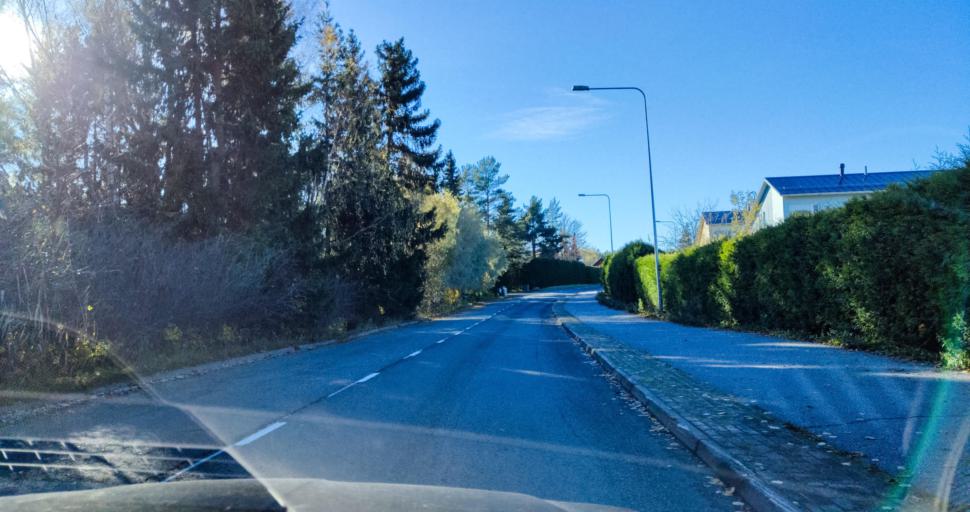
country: FI
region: Varsinais-Suomi
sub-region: Turku
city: Turku
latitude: 60.4083
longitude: 22.2206
